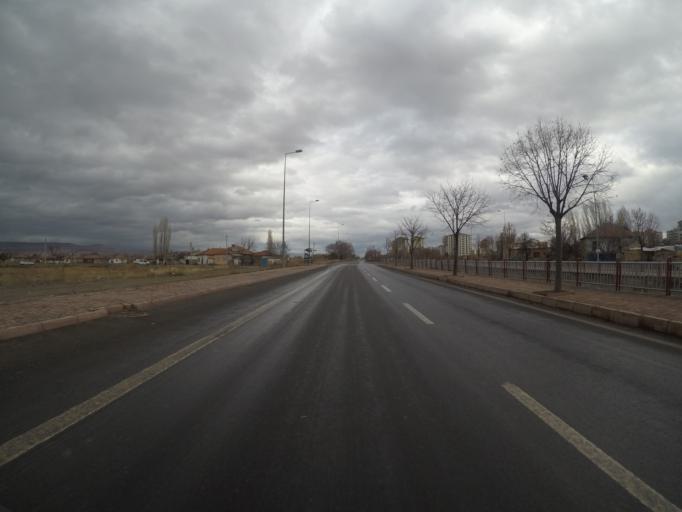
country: TR
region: Kayseri
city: Kayseri
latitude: 38.7551
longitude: 35.4778
